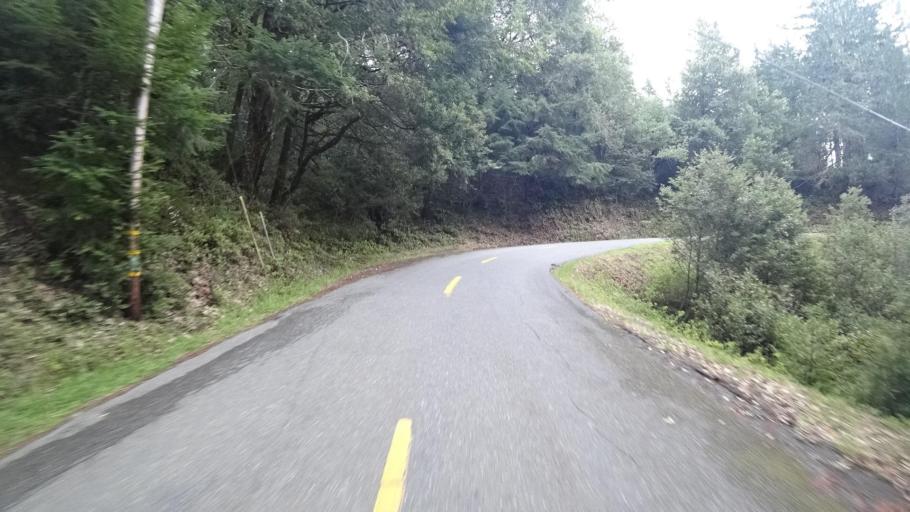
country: US
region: California
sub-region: Humboldt County
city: Bayside
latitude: 40.7500
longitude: -123.9715
